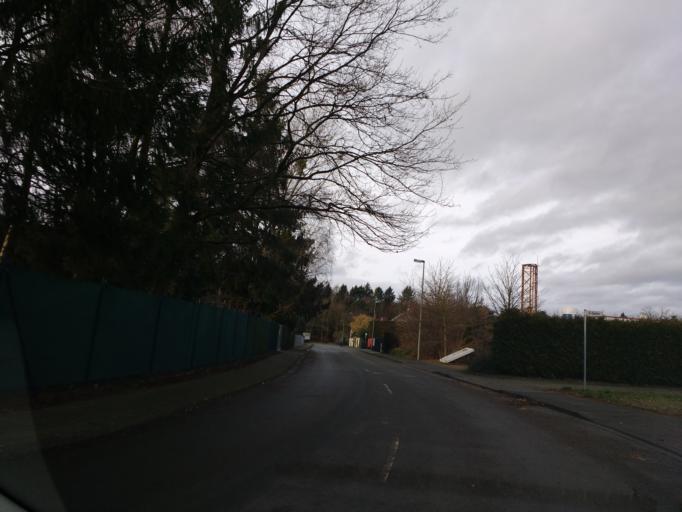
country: DE
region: North Rhine-Westphalia
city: Bad Lippspringe
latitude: 51.7806
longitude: 8.8007
